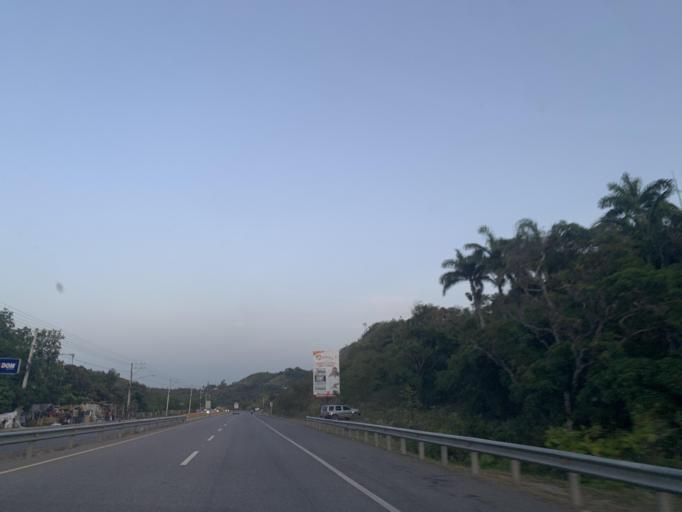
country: DO
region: Puerto Plata
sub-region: Puerto Plata
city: Puerto Plata
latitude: 19.8265
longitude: -70.7479
